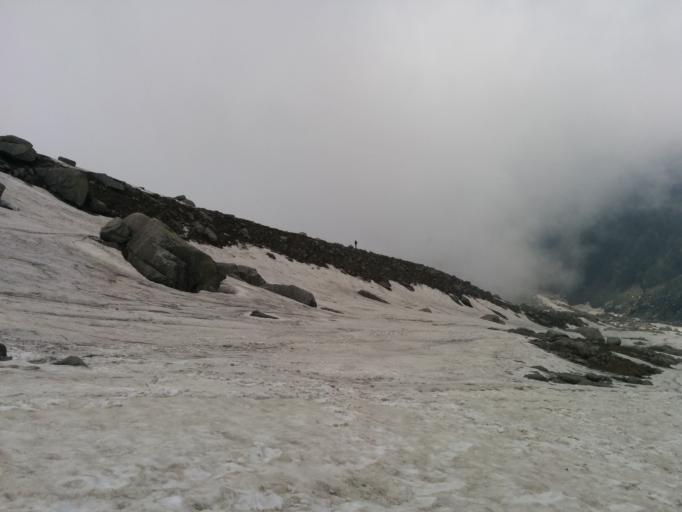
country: IN
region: Himachal Pradesh
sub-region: Kangra
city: Dharmsala
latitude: 32.2847
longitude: 76.3681
